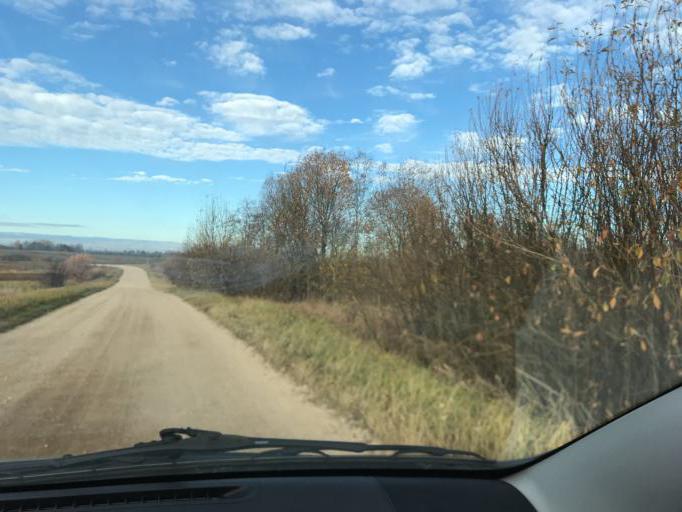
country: BY
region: Vitebsk
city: Haradok
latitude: 55.4532
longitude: 30.0359
